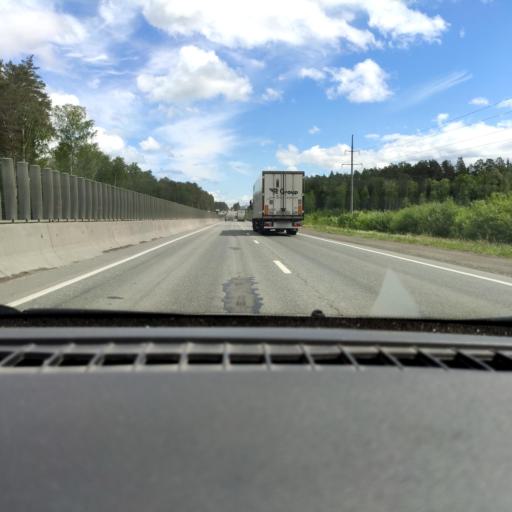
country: RU
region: Perm
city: Overyata
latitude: 58.0378
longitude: 55.9682
